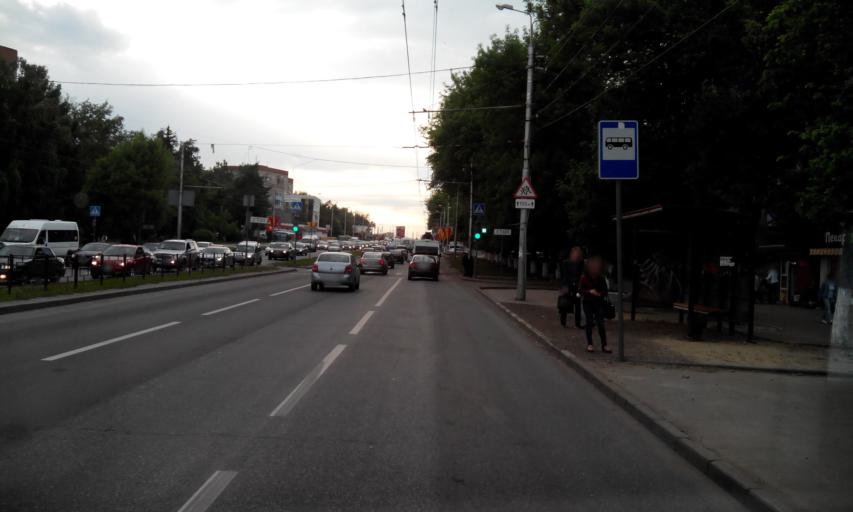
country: RU
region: Penza
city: Penza
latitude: 53.2150
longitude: 44.9864
